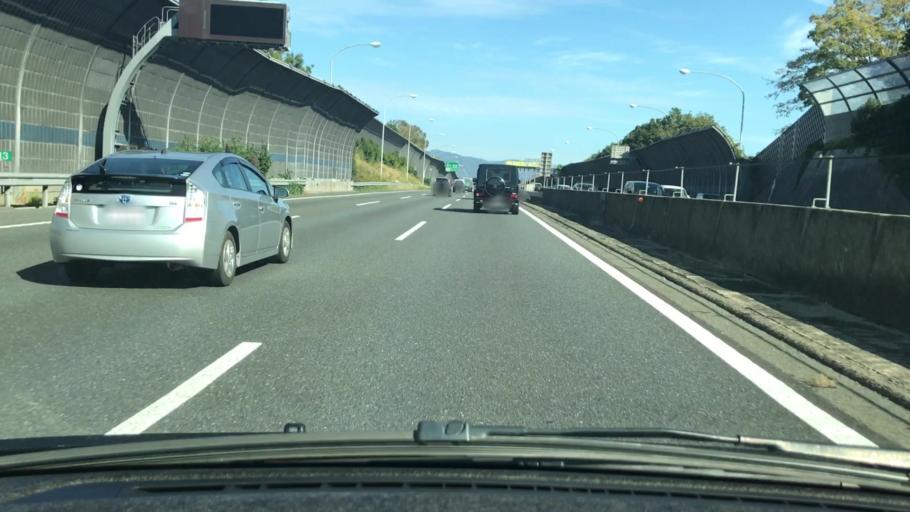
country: JP
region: Osaka
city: Ibaraki
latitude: 34.8201
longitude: 135.5520
